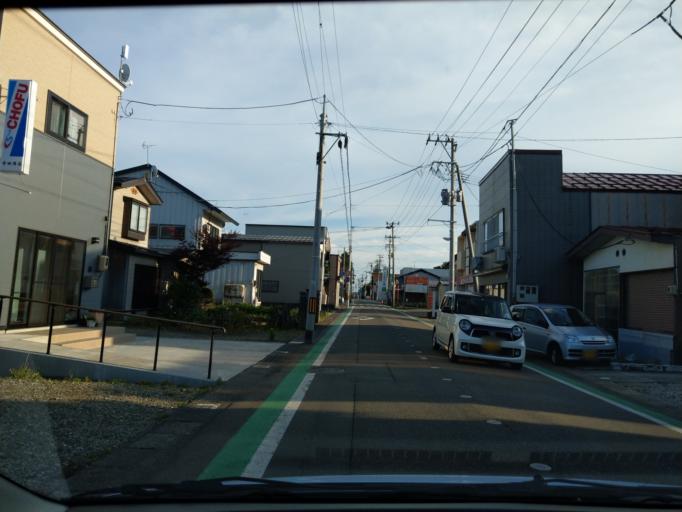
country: JP
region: Akita
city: Omagari
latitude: 39.4257
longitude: 140.5492
